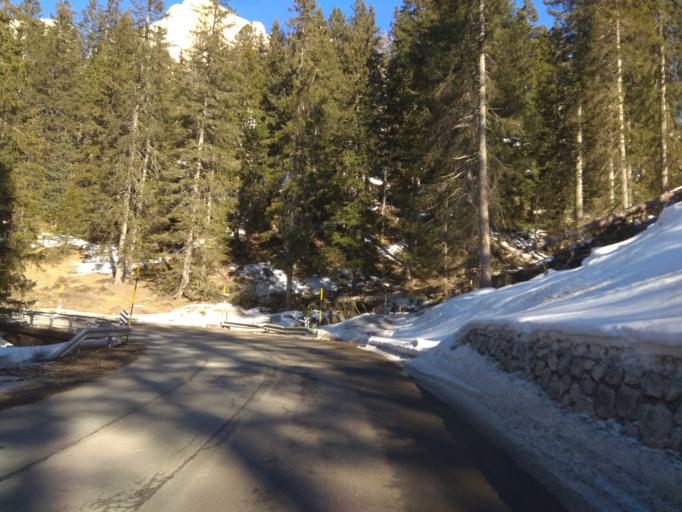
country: IT
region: Trentino-Alto Adige
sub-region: Bolzano
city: Nova Levante
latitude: 46.4166
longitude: 11.6004
